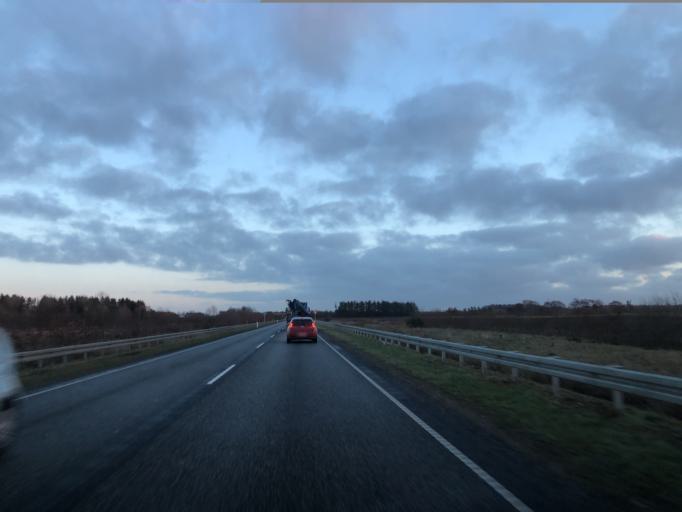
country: DK
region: Central Jutland
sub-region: Herning Kommune
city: Sunds
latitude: 56.1929
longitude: 9.0032
